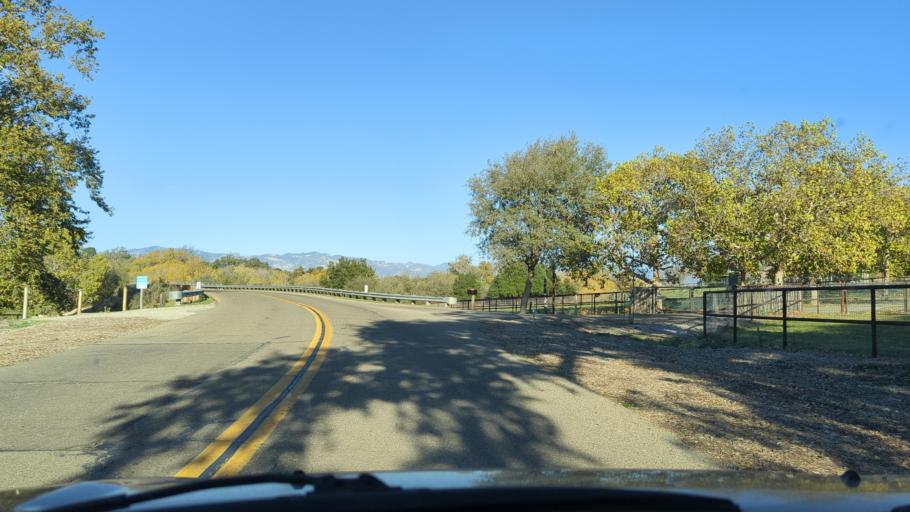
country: US
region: California
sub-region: Santa Barbara County
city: Santa Ynez
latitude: 34.5835
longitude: -120.1015
